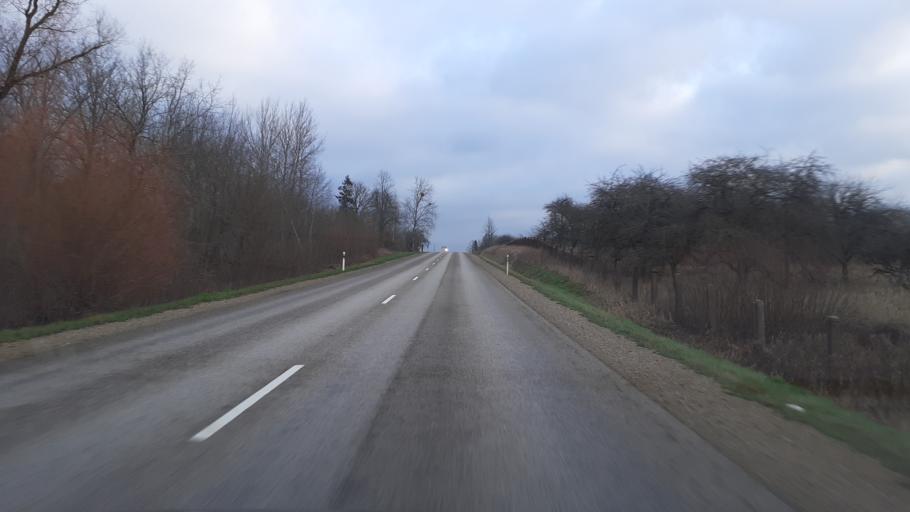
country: LV
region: Durbe
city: Liegi
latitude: 56.6578
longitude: 21.3413
